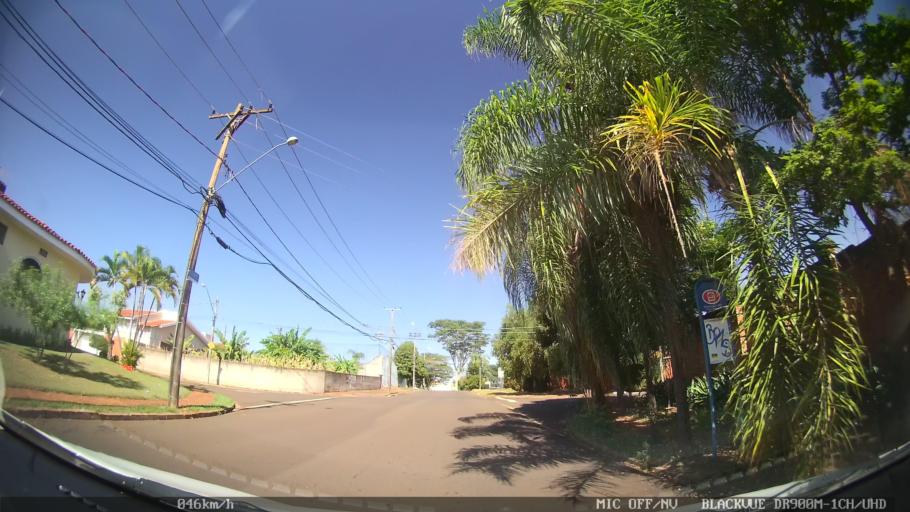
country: BR
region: Sao Paulo
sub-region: Ribeirao Preto
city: Ribeirao Preto
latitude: -21.2013
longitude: -47.7826
